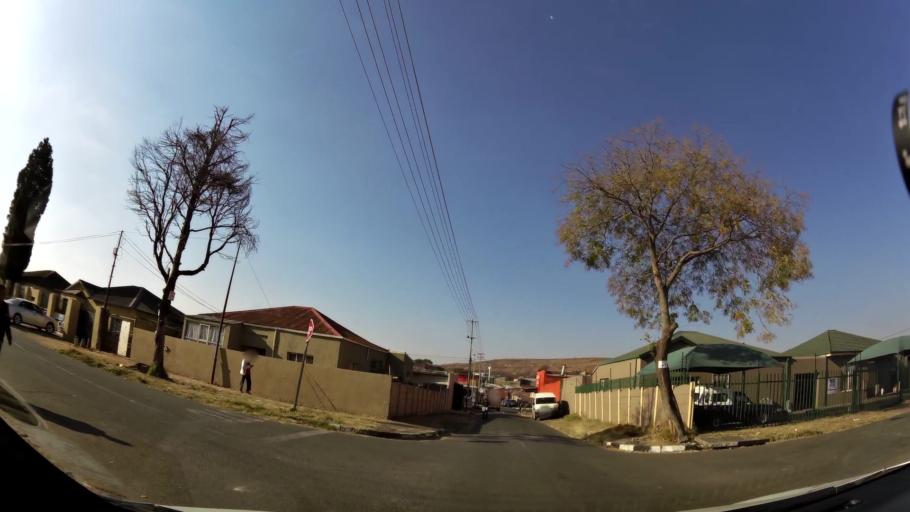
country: ZA
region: Gauteng
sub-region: City of Johannesburg Metropolitan Municipality
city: Johannesburg
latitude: -26.2367
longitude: 28.0250
